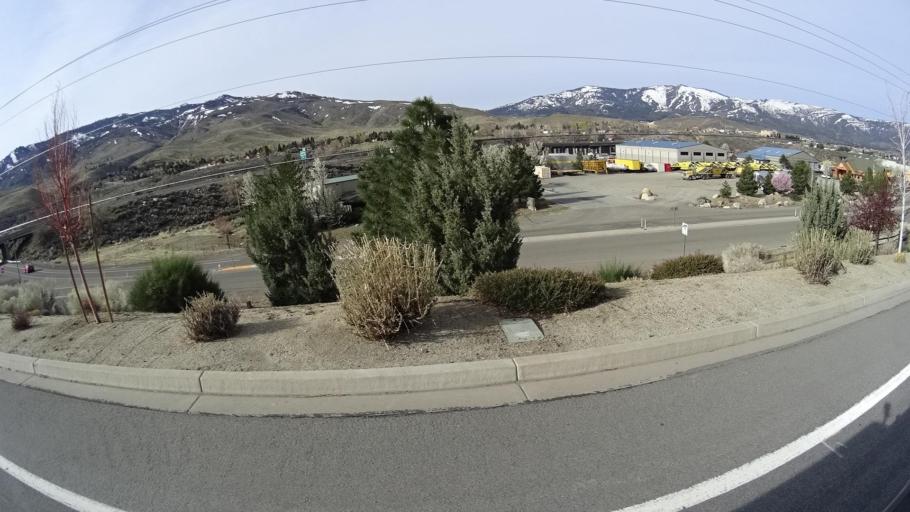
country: US
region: Nevada
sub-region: Washoe County
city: Mogul
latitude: 39.5135
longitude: -119.9495
